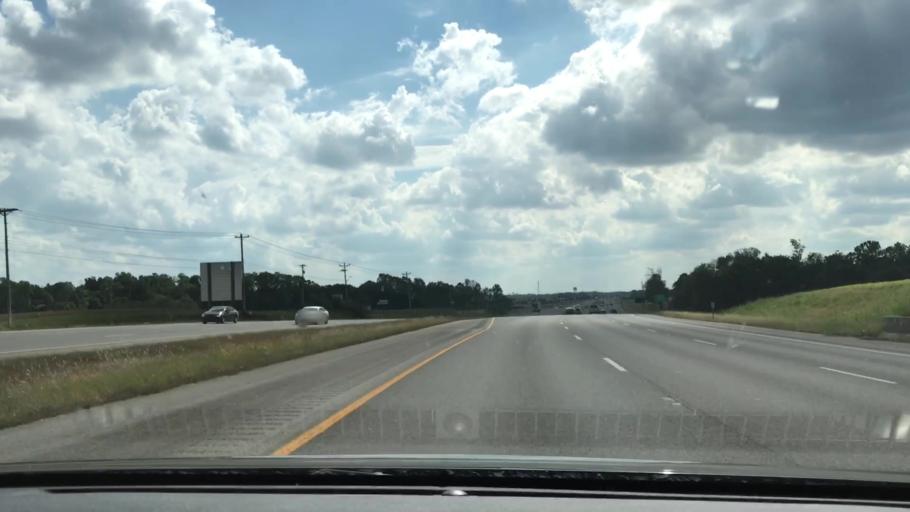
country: US
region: Kentucky
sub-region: Christian County
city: Oak Grove
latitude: 36.6835
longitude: -87.4488
